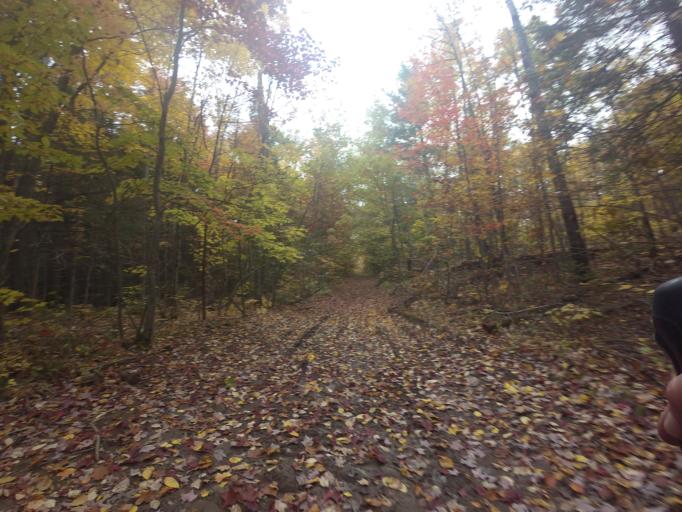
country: CA
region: Ontario
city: Pembroke
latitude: 45.7231
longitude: -77.2246
